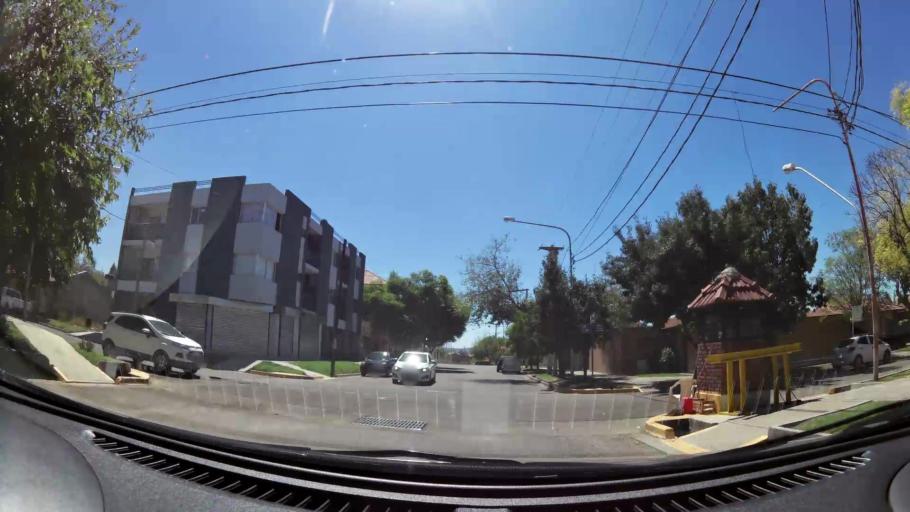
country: AR
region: Mendoza
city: Las Heras
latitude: -32.8523
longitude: -68.8532
